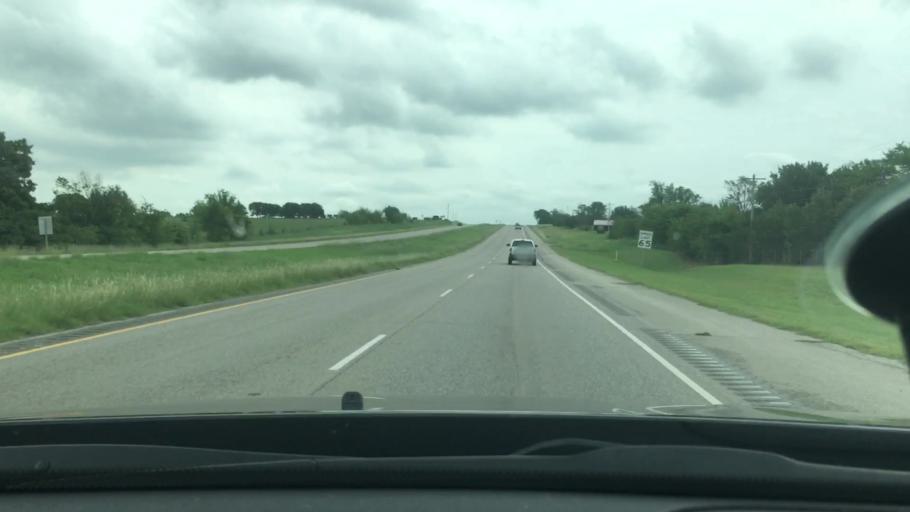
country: US
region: Oklahoma
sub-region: Carter County
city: Wilson
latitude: 34.1729
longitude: -97.4695
